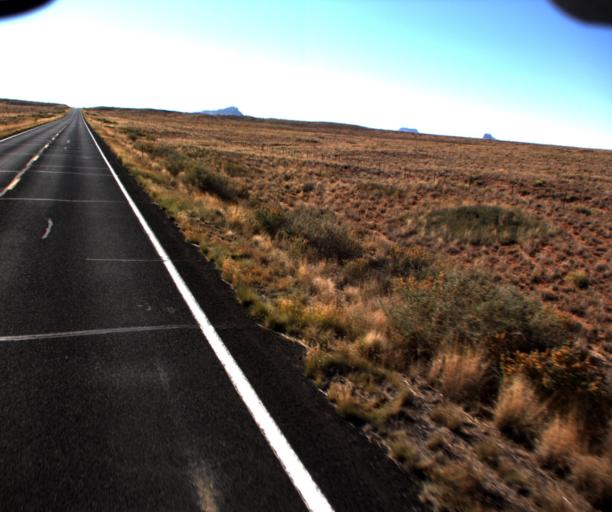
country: US
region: Arizona
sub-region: Navajo County
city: Dilkon
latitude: 35.5607
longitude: -110.4565
